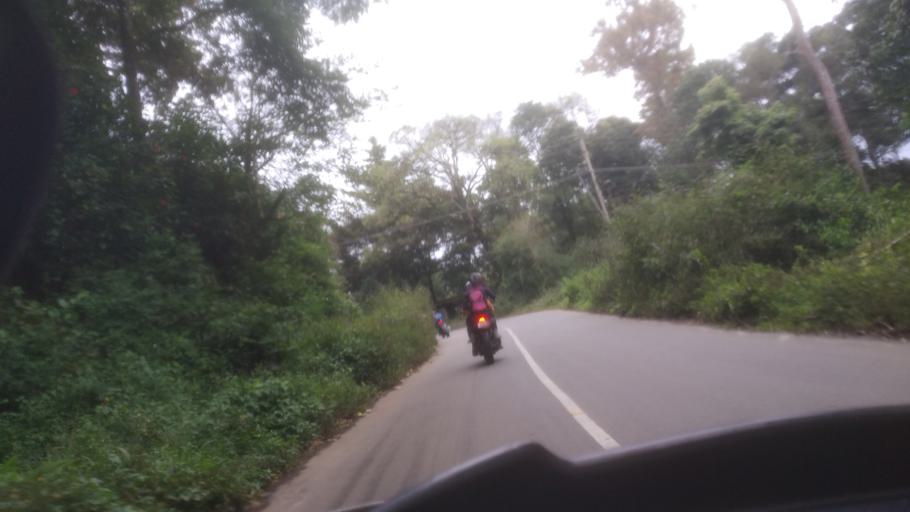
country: IN
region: Tamil Nadu
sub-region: Theni
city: Kombai
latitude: 9.8953
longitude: 77.1616
